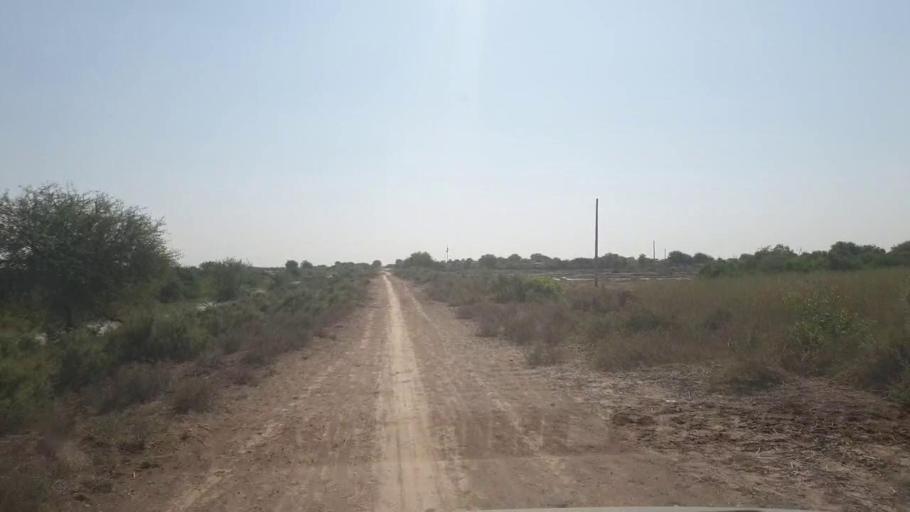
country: PK
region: Sindh
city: Tando Bago
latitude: 24.8931
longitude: 69.1645
